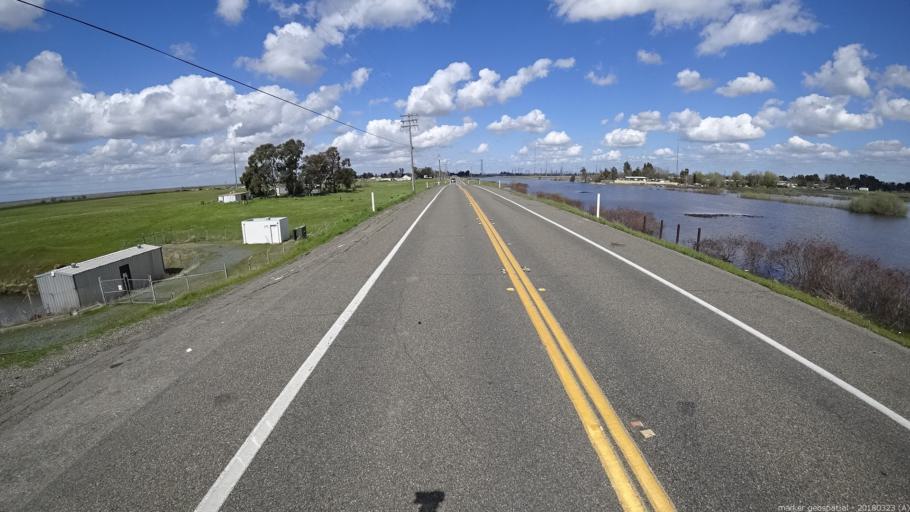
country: US
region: California
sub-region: Sacramento County
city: Elverta
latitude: 38.6966
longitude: -121.4857
